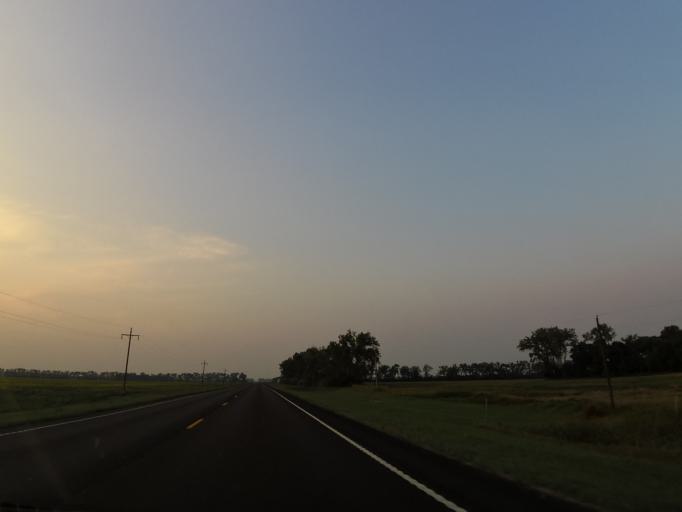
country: US
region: North Dakota
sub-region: Walsh County
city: Park River
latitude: 48.3339
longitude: -97.6224
